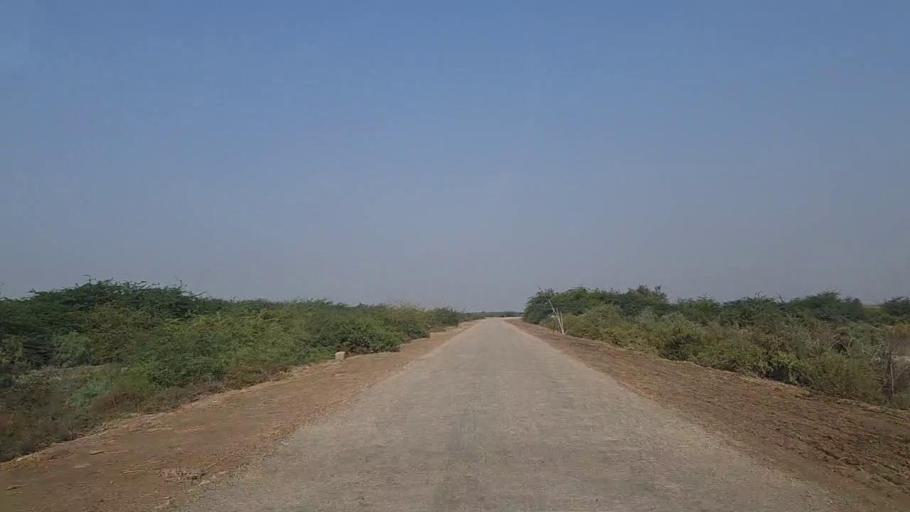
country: PK
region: Sindh
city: Keti Bandar
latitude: 24.2380
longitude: 67.6837
